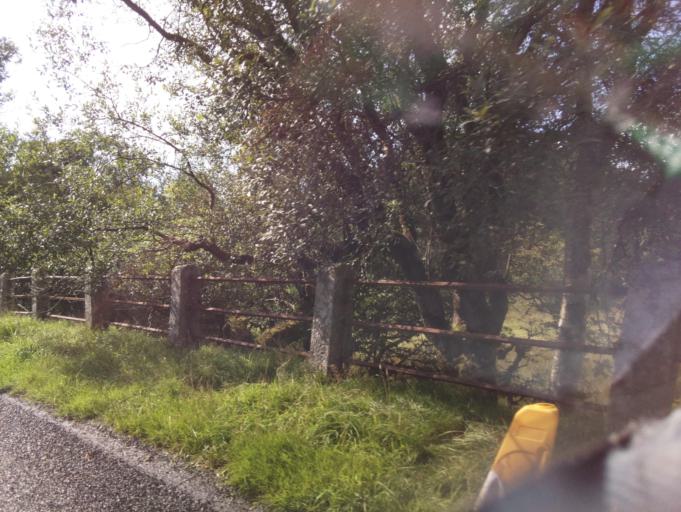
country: GB
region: England
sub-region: Devon
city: Yelverton
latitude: 50.5582
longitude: -3.9671
